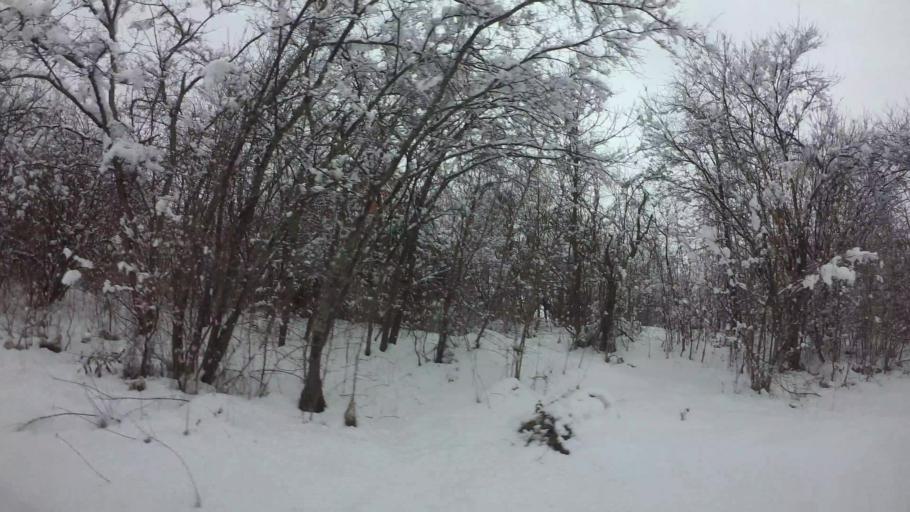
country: BA
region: Federation of Bosnia and Herzegovina
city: Hadzici
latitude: 43.8550
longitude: 18.2582
